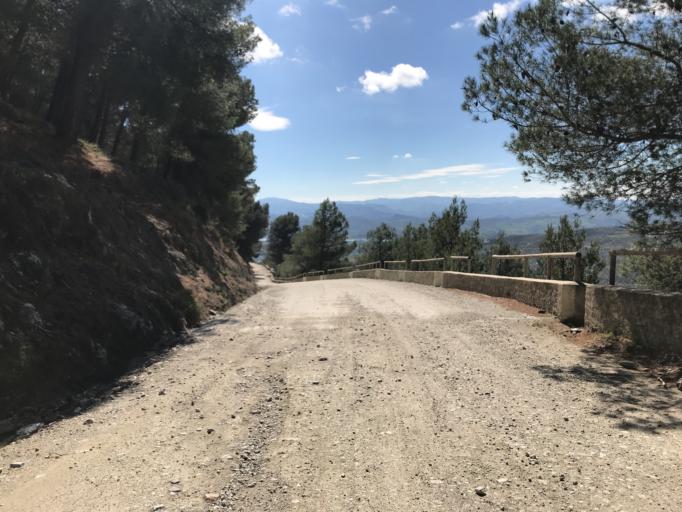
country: ES
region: Andalusia
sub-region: Provincia de Malaga
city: Alcaucin
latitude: 36.9127
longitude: -4.1040
